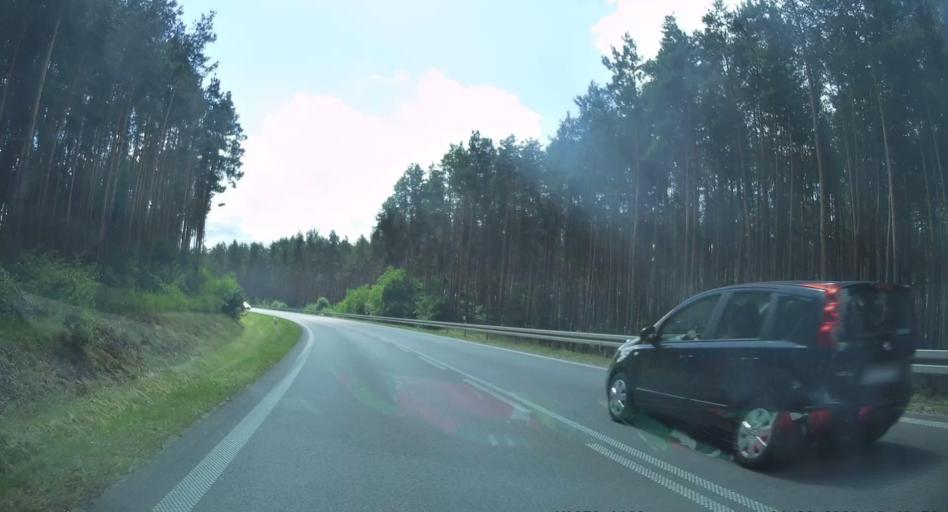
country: PL
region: Subcarpathian Voivodeship
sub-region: Powiat mielecki
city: Padew Narodowa
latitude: 50.3597
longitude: 21.4833
